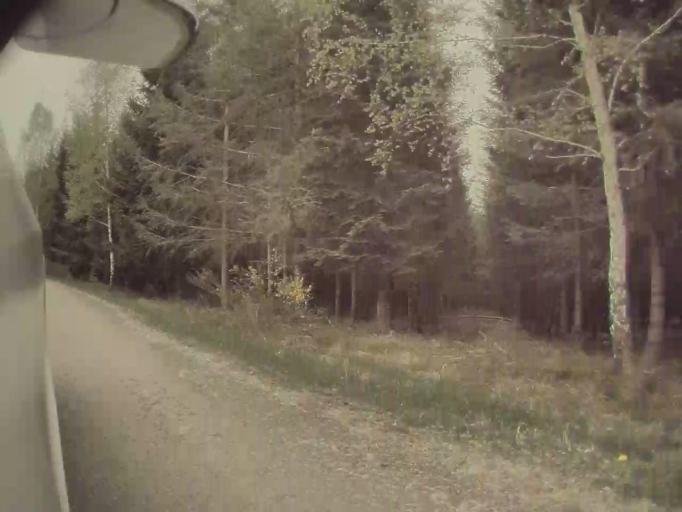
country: BE
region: Wallonia
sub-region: Province du Luxembourg
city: La Roche-en-Ardenne
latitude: 50.2322
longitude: 5.5968
